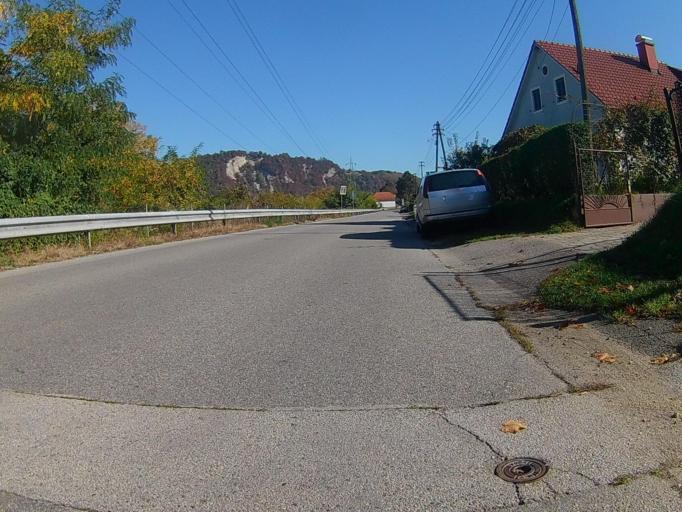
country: SI
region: Maribor
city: Maribor
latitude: 46.5554
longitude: 15.6667
